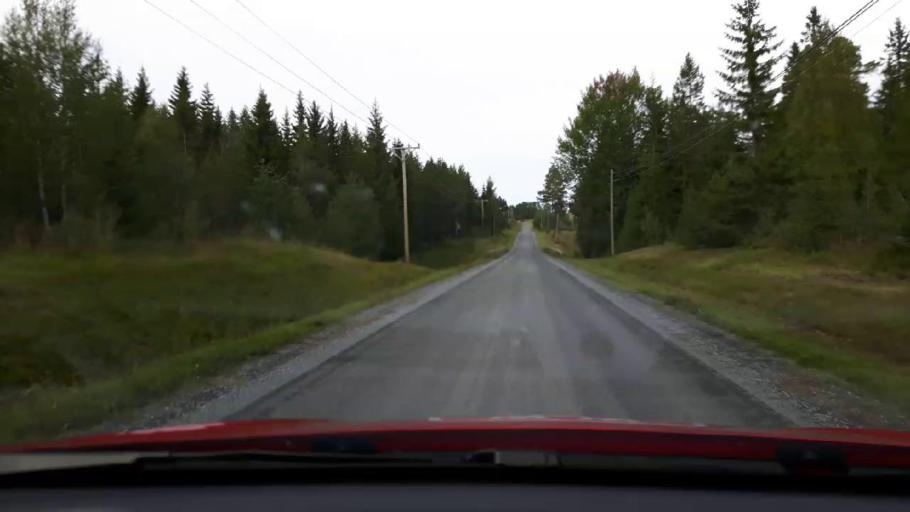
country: SE
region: Jaemtland
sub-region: Krokoms Kommun
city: Valla
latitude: 63.2508
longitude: 13.9561
